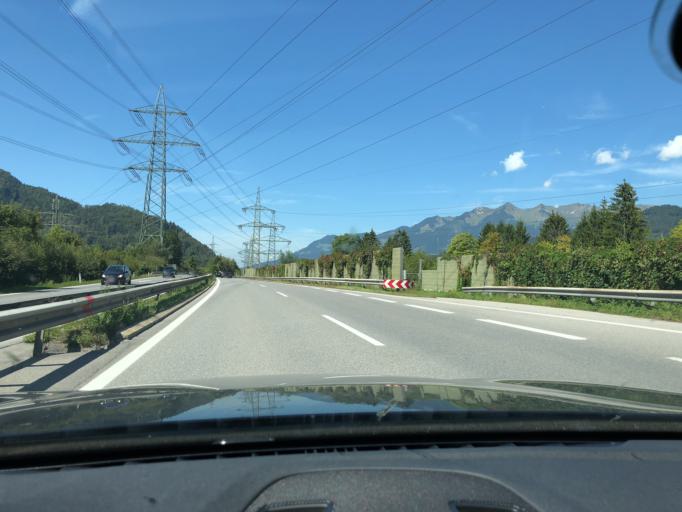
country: AT
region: Vorarlberg
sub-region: Politischer Bezirk Bludenz
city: Bludenz
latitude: 47.1532
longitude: 9.8118
